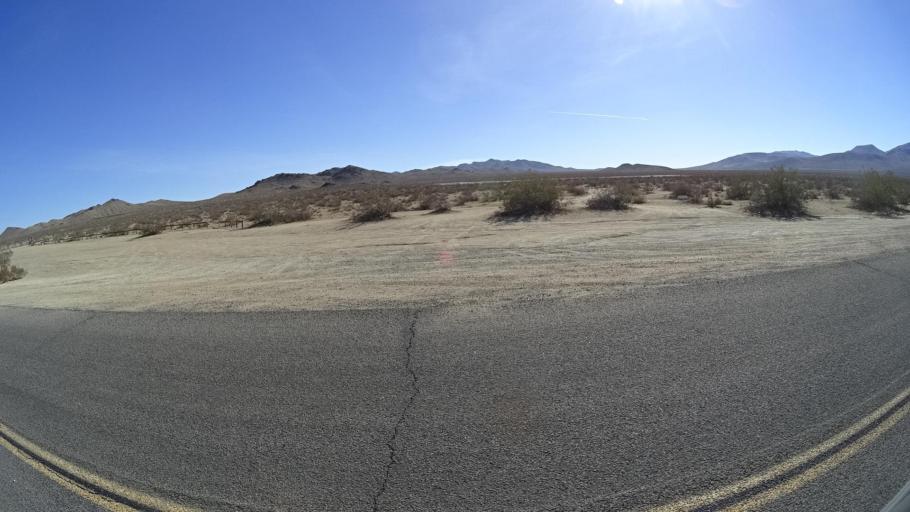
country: US
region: California
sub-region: Kern County
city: Ridgecrest
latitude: 35.5501
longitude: -117.7156
